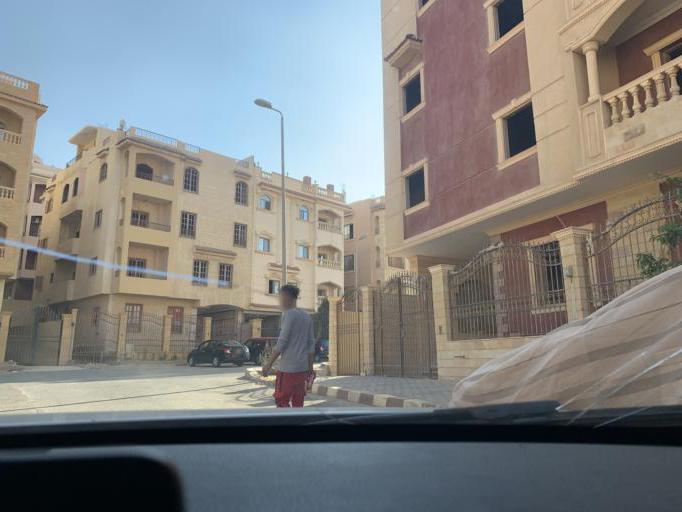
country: EG
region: Muhafazat al Qalyubiyah
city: Al Khankah
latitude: 30.0020
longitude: 31.4866
